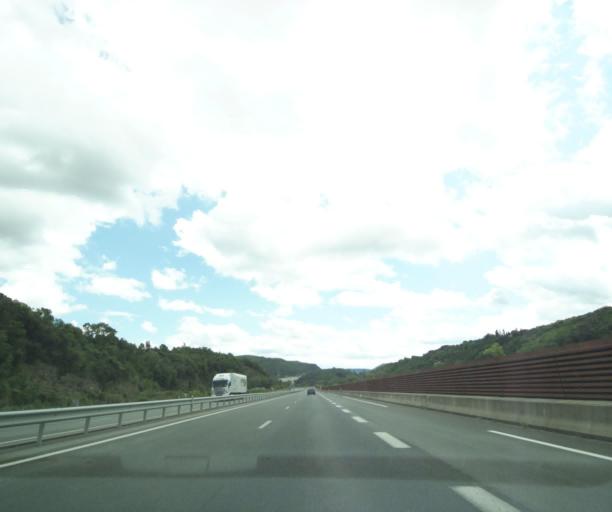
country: FR
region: Languedoc-Roussillon
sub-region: Departement de l'Herault
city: Lodeve
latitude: 43.7578
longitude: 3.3293
